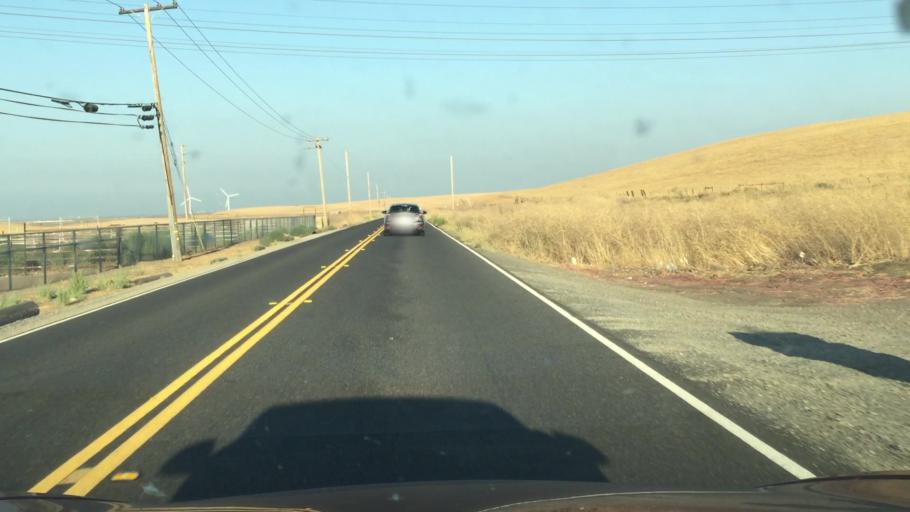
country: US
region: California
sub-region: San Joaquin County
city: Mountain House
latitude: 37.7133
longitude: -121.5507
